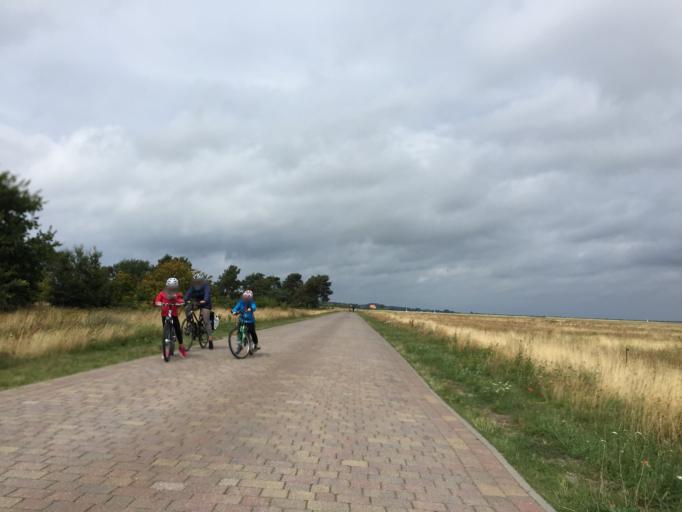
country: DE
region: Mecklenburg-Vorpommern
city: Hiddensee
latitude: 54.5552
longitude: 13.1077
